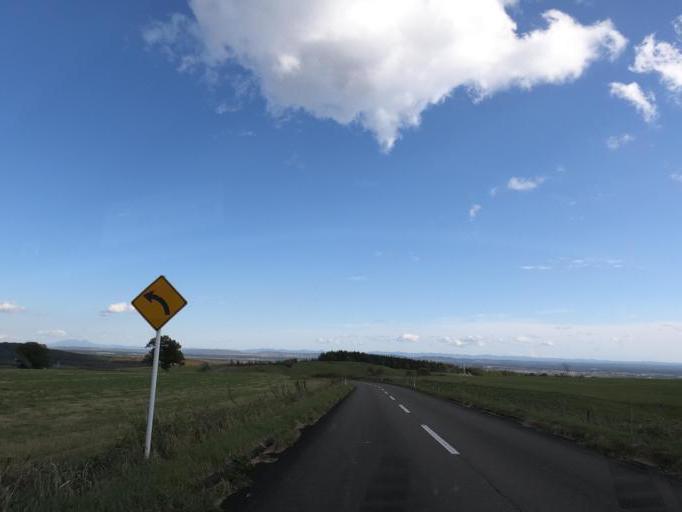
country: JP
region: Hokkaido
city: Otofuke
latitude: 43.2775
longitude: 143.2291
